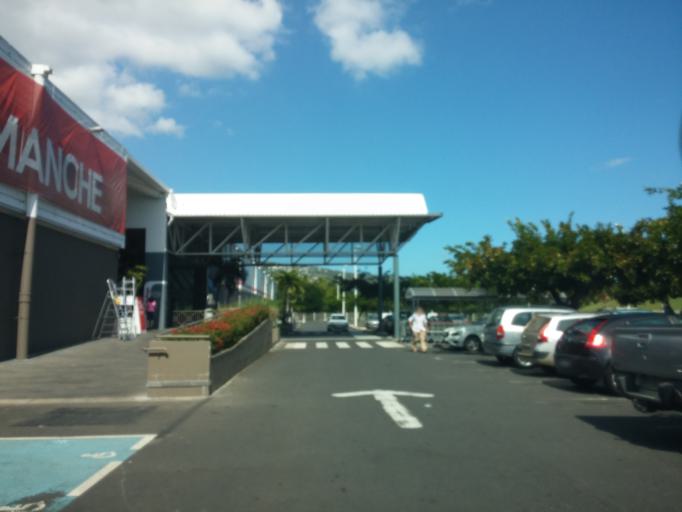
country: RE
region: Reunion
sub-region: Reunion
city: Saint-Paul
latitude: -20.9865
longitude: 55.2914
